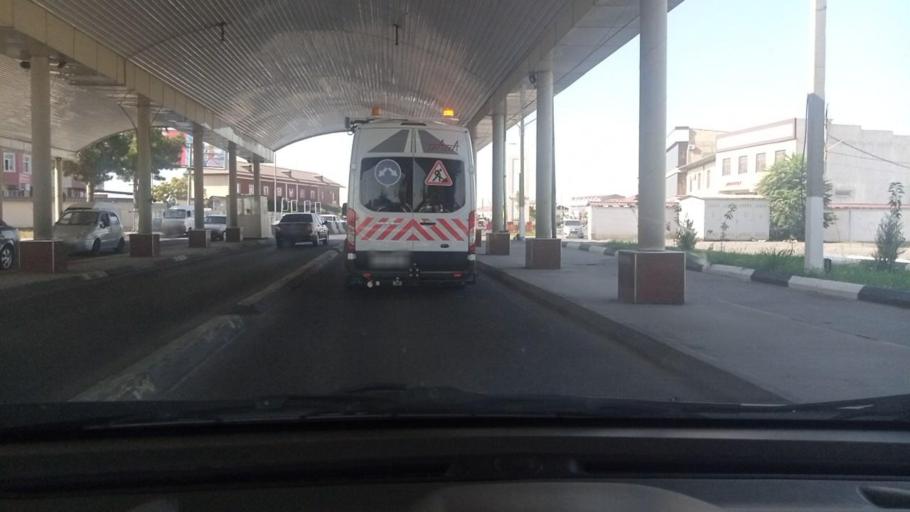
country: UZ
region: Toshkent Shahri
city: Bektemir
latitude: 41.2262
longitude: 69.3354
